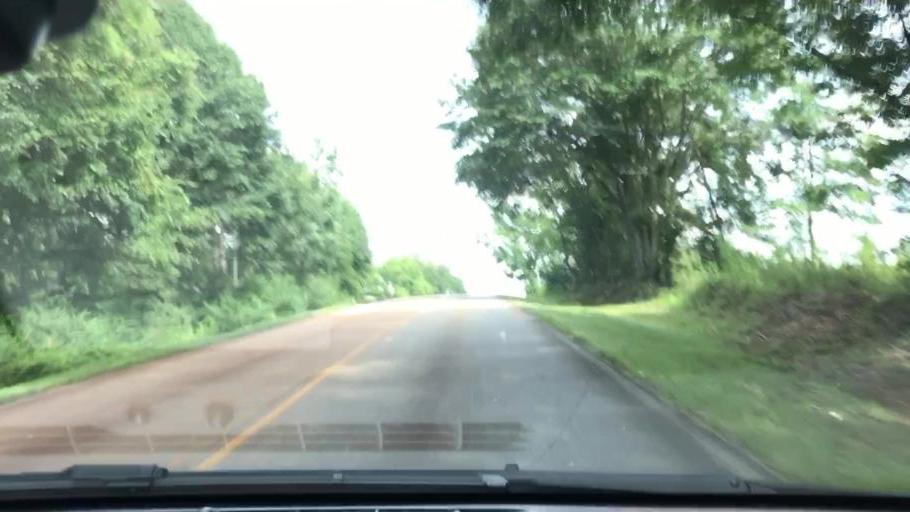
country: US
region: Georgia
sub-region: Clay County
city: Fort Gaines
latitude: 31.5693
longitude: -84.9962
